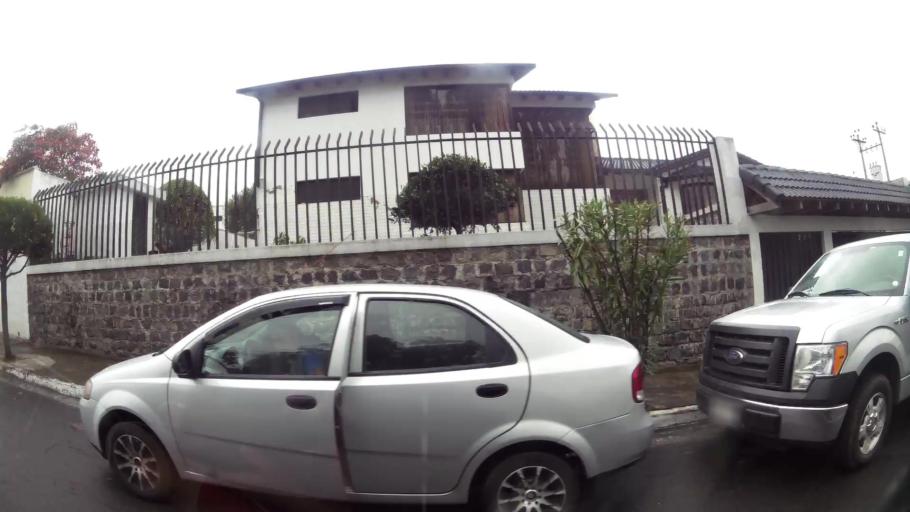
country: EC
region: Pichincha
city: Sangolqui
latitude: -0.3188
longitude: -78.4361
